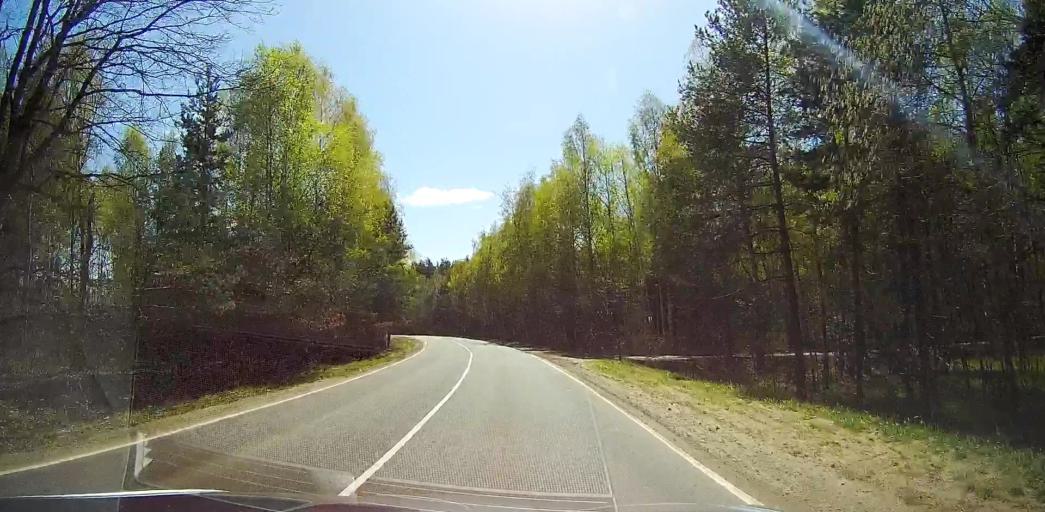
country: RU
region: Moskovskaya
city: Beloozerskiy
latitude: 55.4913
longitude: 38.4270
